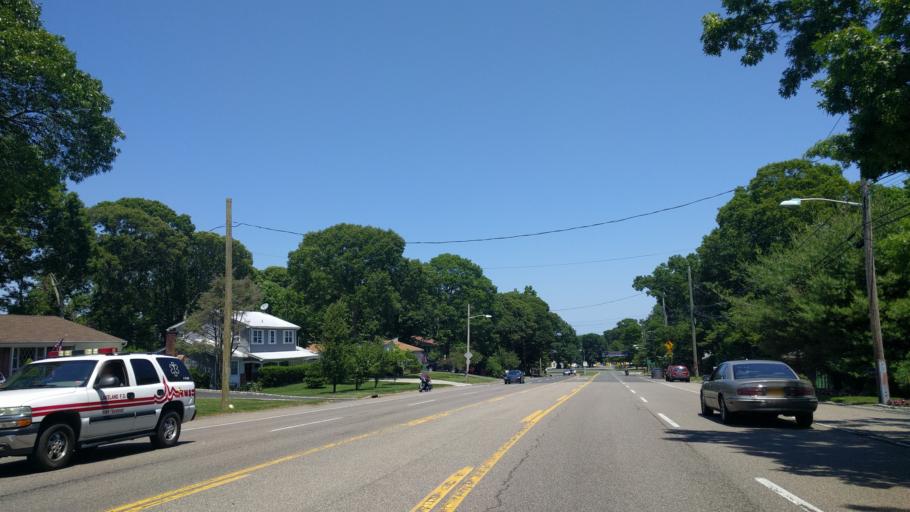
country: US
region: New York
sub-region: Suffolk County
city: Ronkonkoma
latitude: 40.8186
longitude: -73.1257
